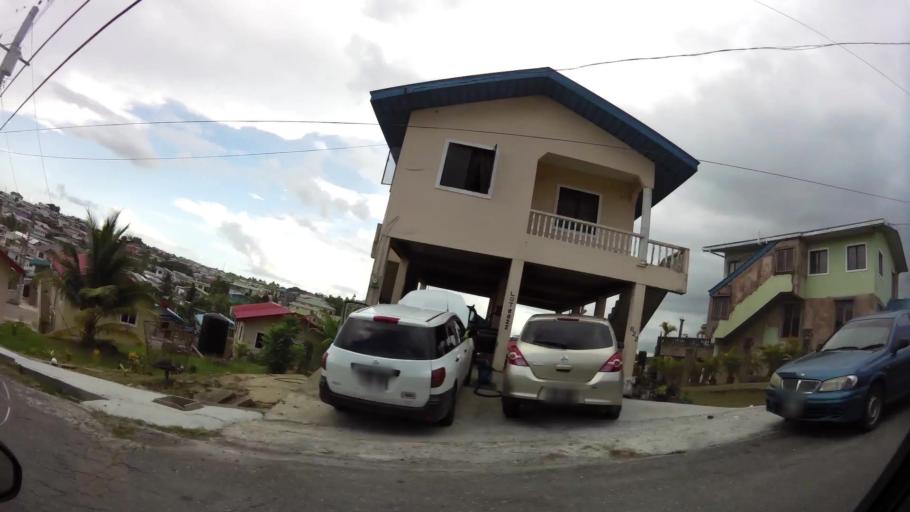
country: TT
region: City of San Fernando
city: Mon Repos
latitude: 10.2558
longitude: -61.4590
